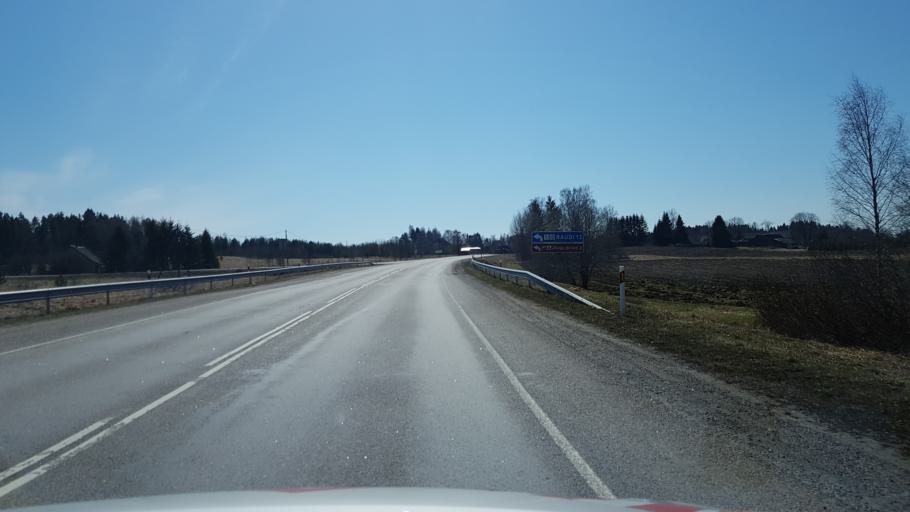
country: EE
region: Ida-Virumaa
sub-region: Johvi vald
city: Johvi
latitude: 59.1480
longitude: 27.3586
